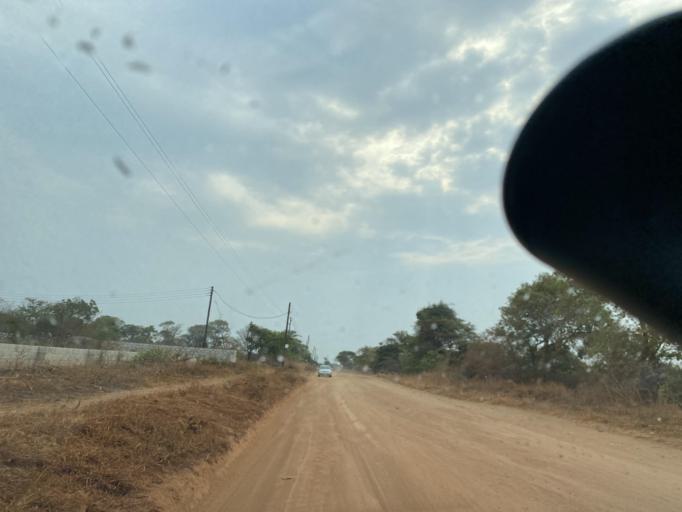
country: ZM
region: Lusaka
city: Lusaka
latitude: -15.2896
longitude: 28.2812
